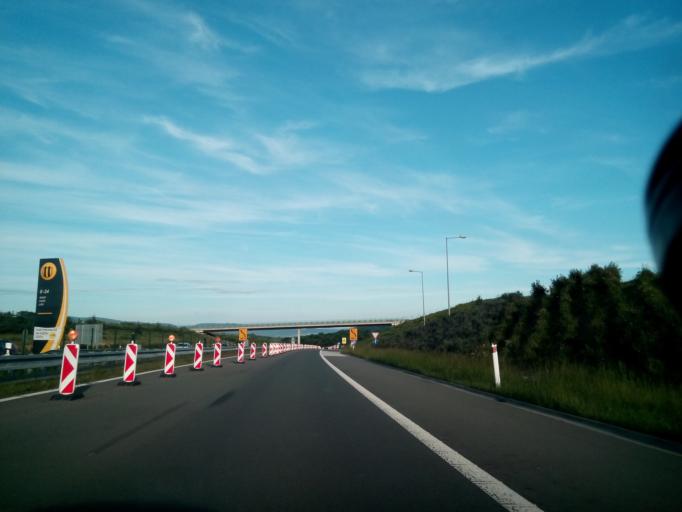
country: SK
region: Presovsky
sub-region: Okres Presov
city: Presov
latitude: 49.0004
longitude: 21.1866
